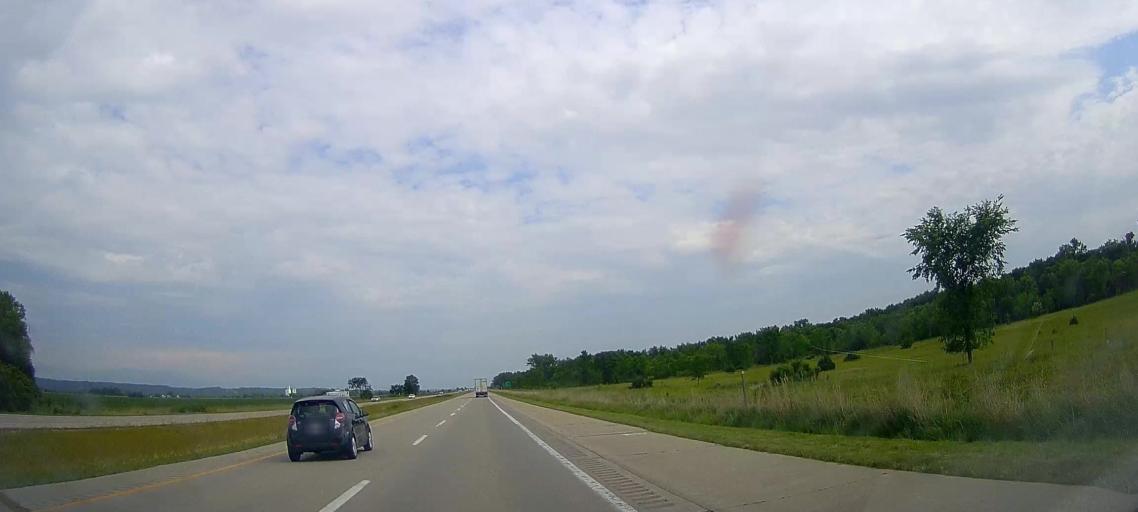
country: US
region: Nebraska
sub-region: Burt County
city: Tekamah
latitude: 41.8196
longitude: -96.0714
